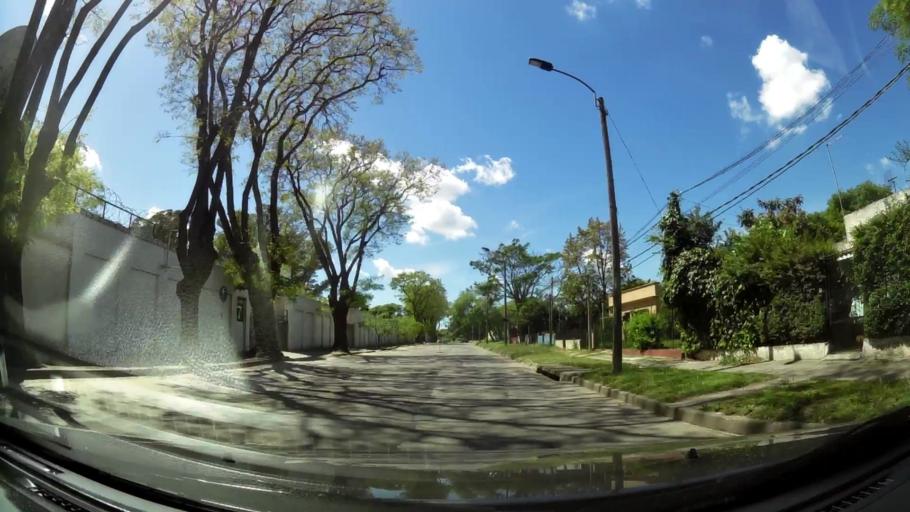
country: UY
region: Montevideo
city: Montevideo
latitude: -34.8434
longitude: -56.1414
